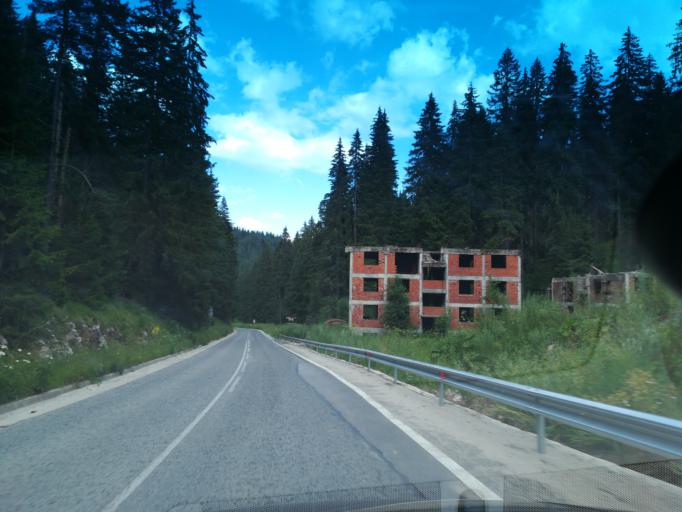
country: BG
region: Smolyan
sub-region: Obshtina Smolyan
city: Smolyan
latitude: 41.6585
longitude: 24.7066
